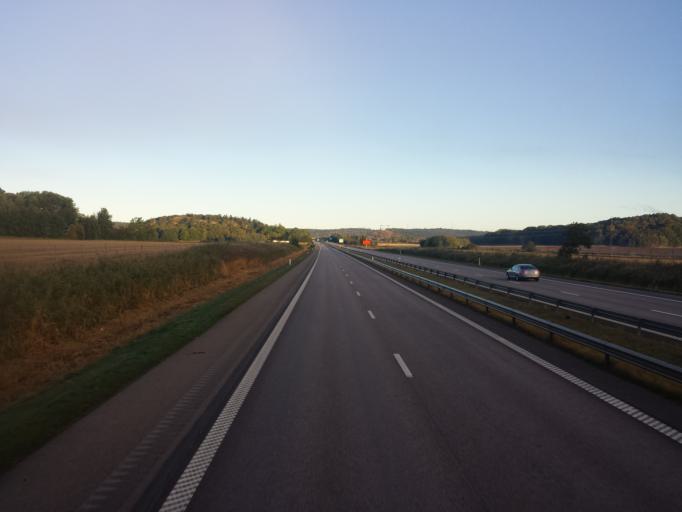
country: SE
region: Halland
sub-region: Kungsbacka Kommun
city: Kungsbacka
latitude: 57.4558
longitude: 12.0883
